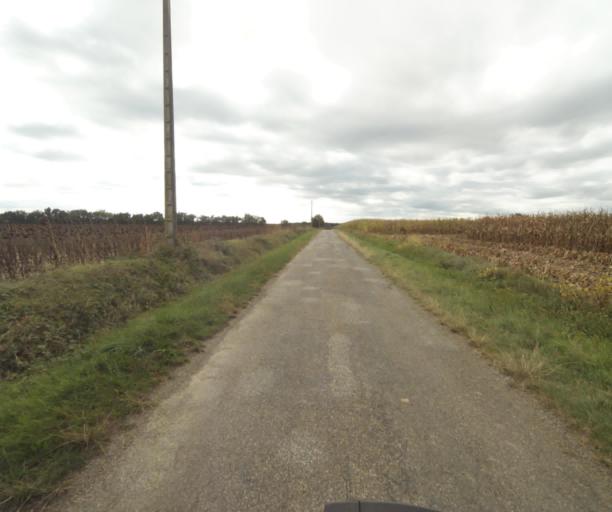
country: FR
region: Midi-Pyrenees
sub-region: Departement du Tarn-et-Garonne
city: Verdun-sur-Garonne
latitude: 43.8694
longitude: 1.1623
